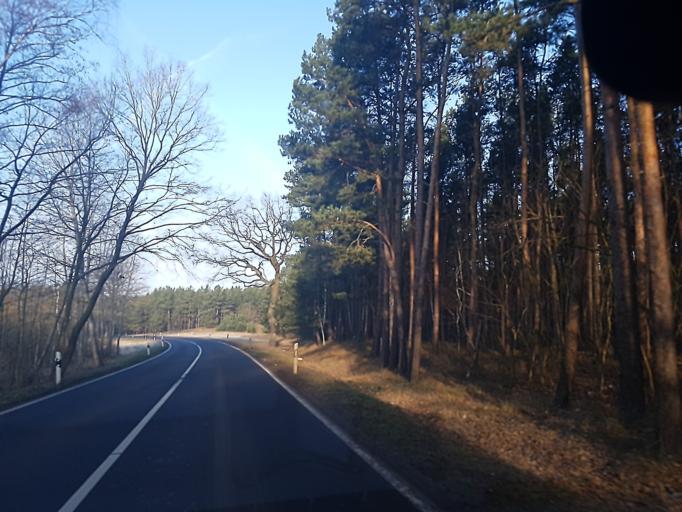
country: DE
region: Brandenburg
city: Golzow
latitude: 52.2778
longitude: 12.6192
